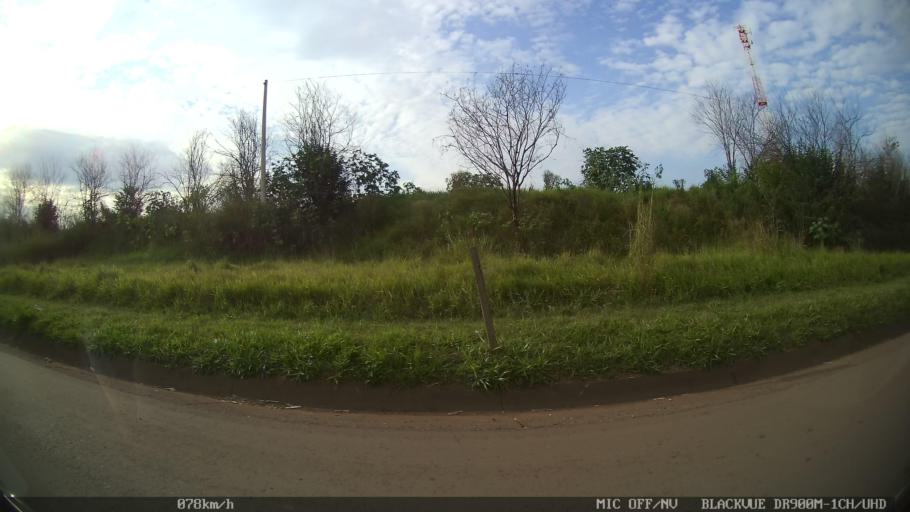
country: BR
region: Sao Paulo
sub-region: Cosmopolis
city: Cosmopolis
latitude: -22.6127
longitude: -47.2296
